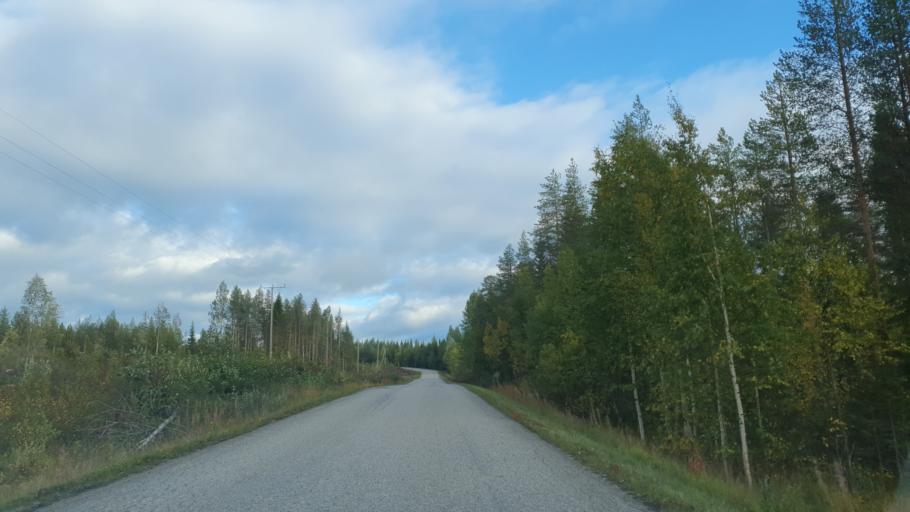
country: FI
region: Kainuu
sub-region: Kehys-Kainuu
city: Kuhmo
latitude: 63.9263
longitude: 30.0098
